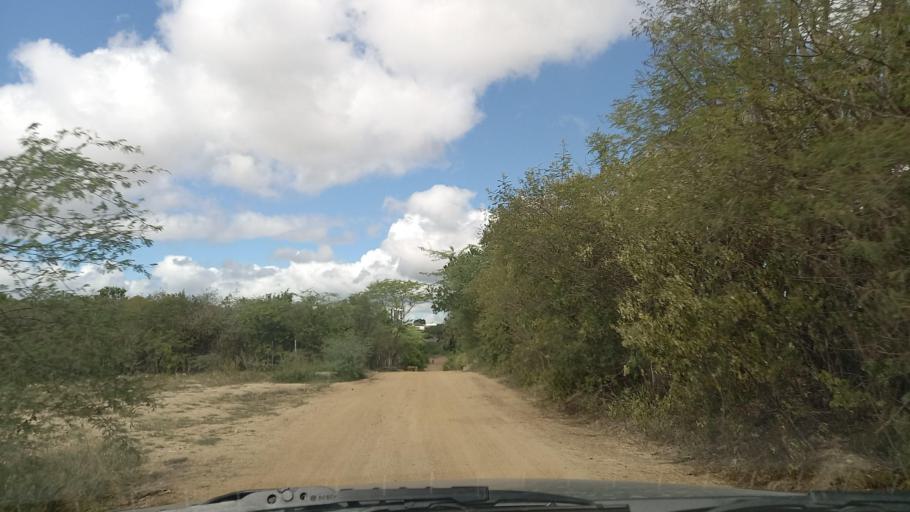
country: BR
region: Pernambuco
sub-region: Caruaru
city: Caruaru
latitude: -8.2500
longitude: -35.9815
